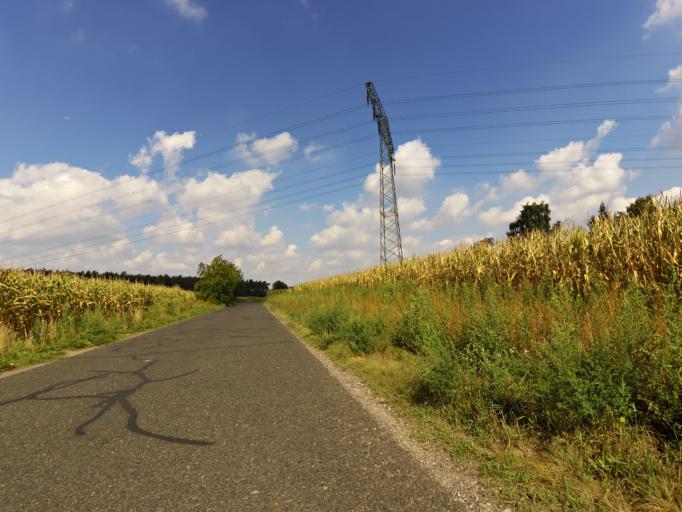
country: DE
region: Berlin
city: Lichtenrade
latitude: 52.3529
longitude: 13.4004
